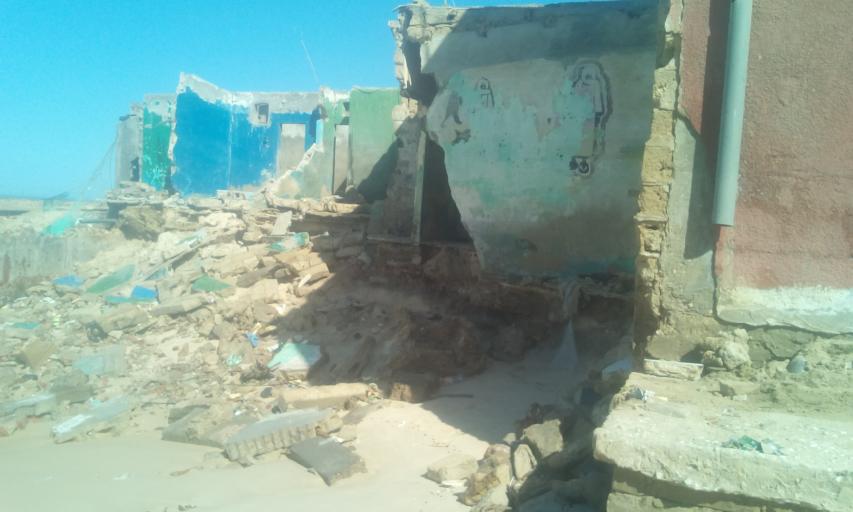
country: SN
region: Saint-Louis
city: Saint-Louis
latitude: 16.0282
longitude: -16.5091
